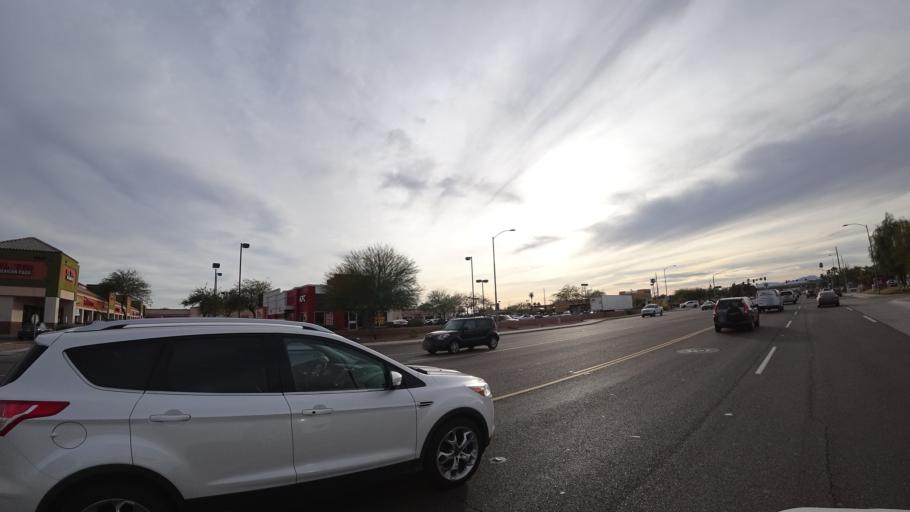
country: US
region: Arizona
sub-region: Maricopa County
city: Peoria
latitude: 33.5664
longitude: -112.2529
